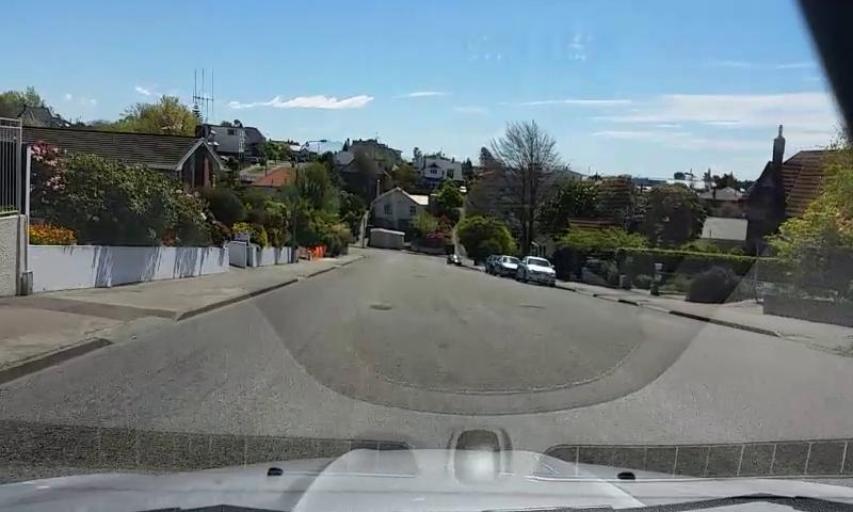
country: NZ
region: Canterbury
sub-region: Timaru District
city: Timaru
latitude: -44.3903
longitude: 171.2406
